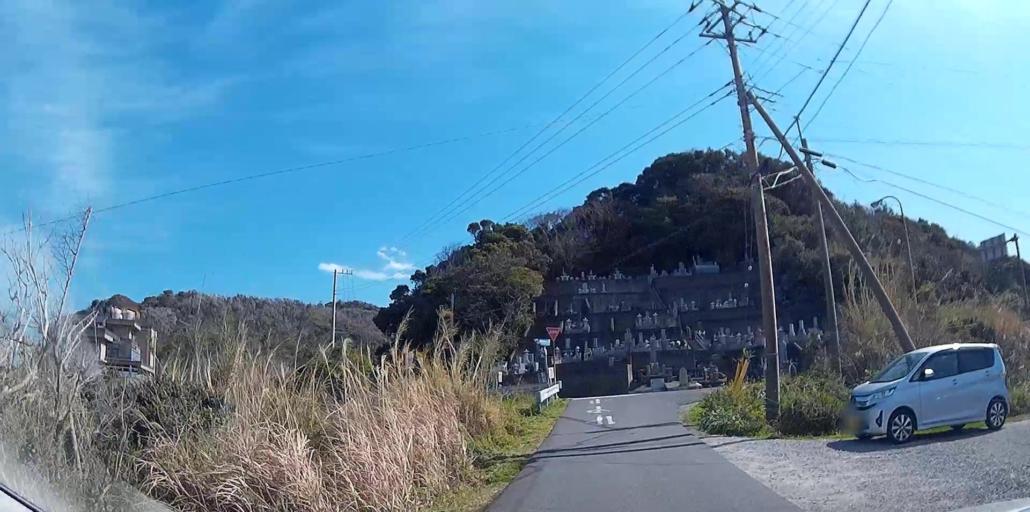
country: JP
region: Chiba
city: Tateyama
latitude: 34.9740
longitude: 139.7582
